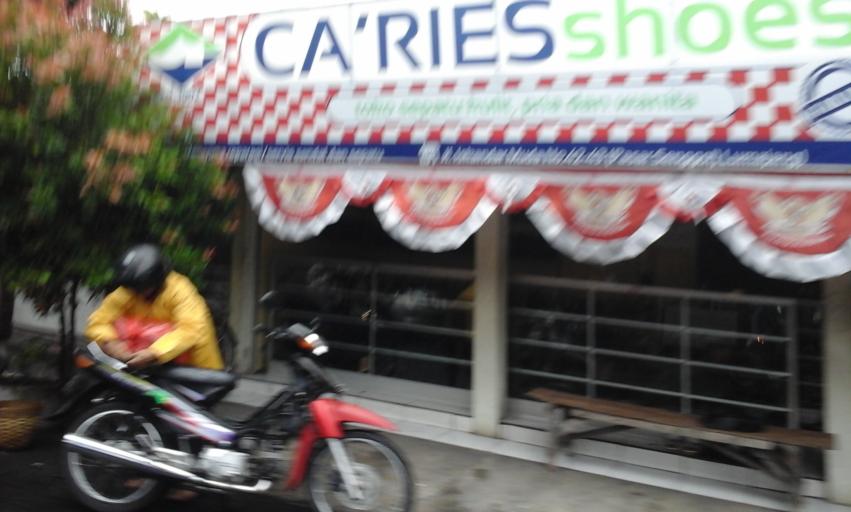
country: ID
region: East Java
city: Lumajang
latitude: -8.1314
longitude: 113.2217
